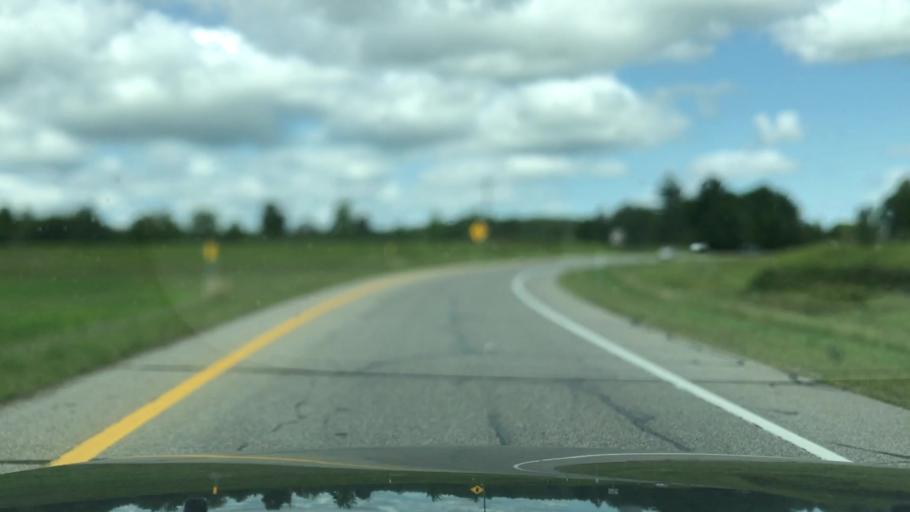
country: US
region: Michigan
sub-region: Mecosta County
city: Big Rapids
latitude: 43.6900
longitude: -85.5211
